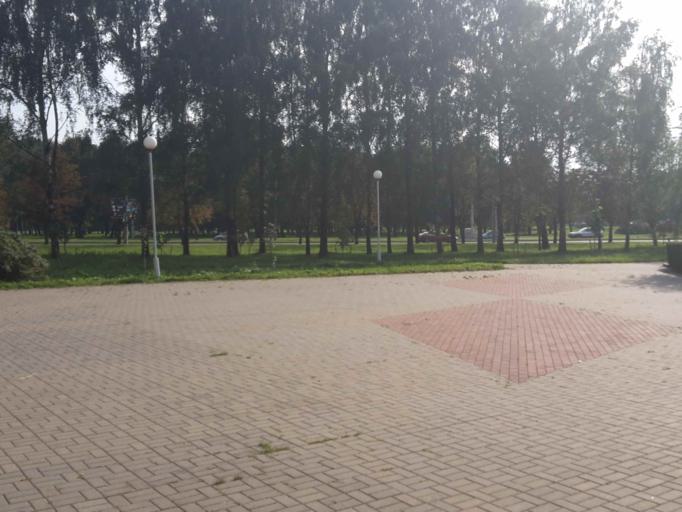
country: BY
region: Minsk
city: Minsk
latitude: 53.9329
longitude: 27.5677
